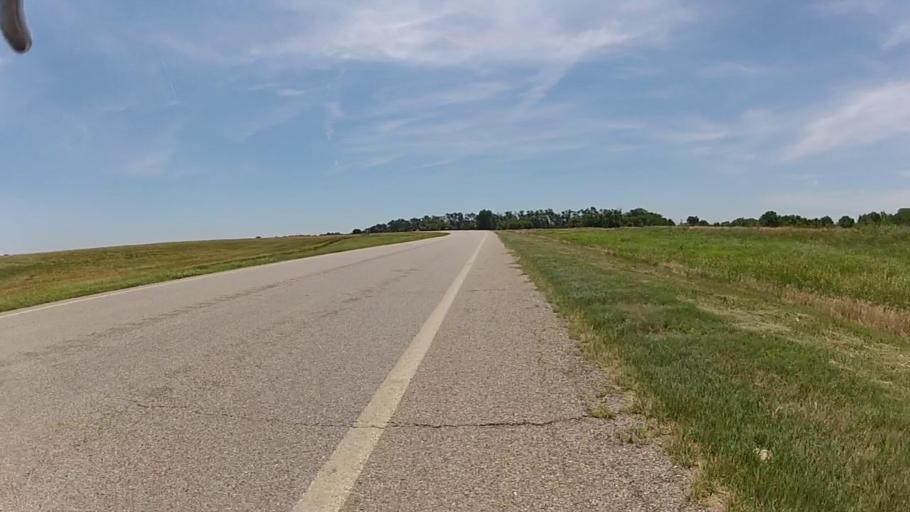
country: US
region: Kansas
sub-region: Barber County
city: Medicine Lodge
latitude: 37.2573
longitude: -98.5245
